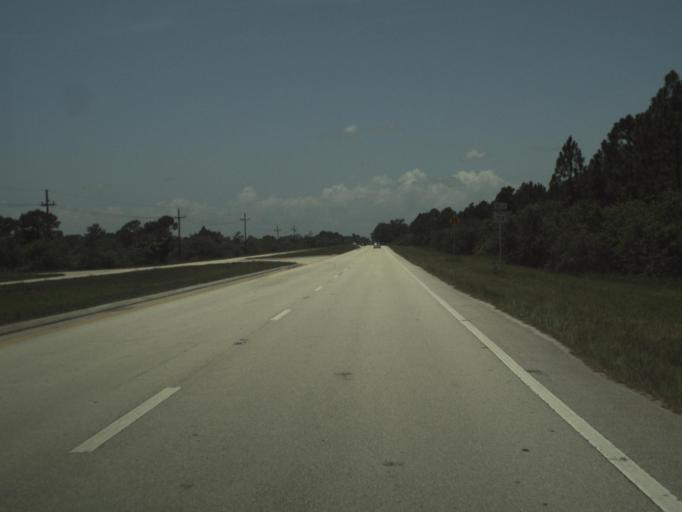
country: US
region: Florida
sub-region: Martin County
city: Palm City
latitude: 27.1618
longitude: -80.3956
